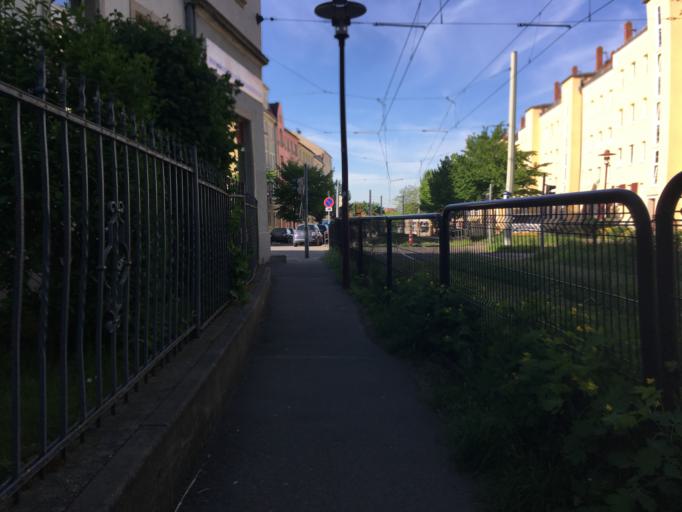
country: DE
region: Saxony
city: Dresden
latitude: 51.0505
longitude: 13.6823
